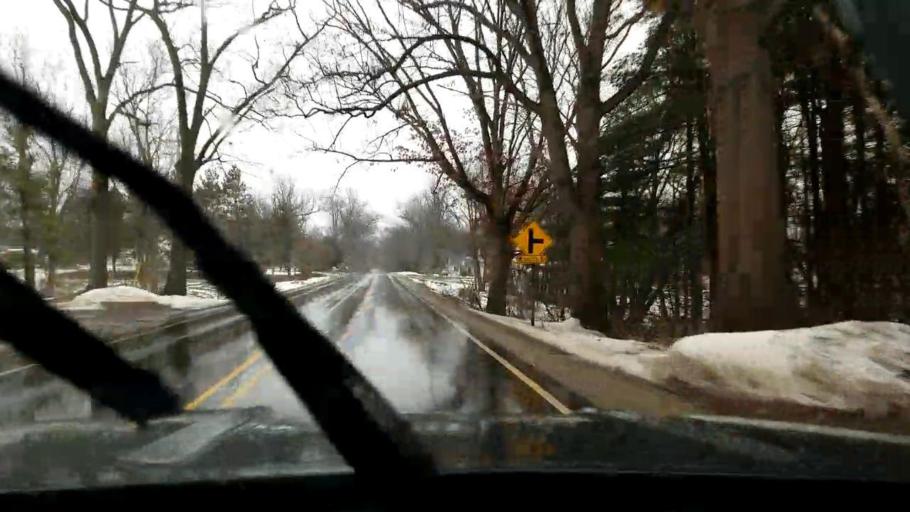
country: US
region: Michigan
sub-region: Jackson County
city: Michigan Center
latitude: 42.2841
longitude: -84.3556
